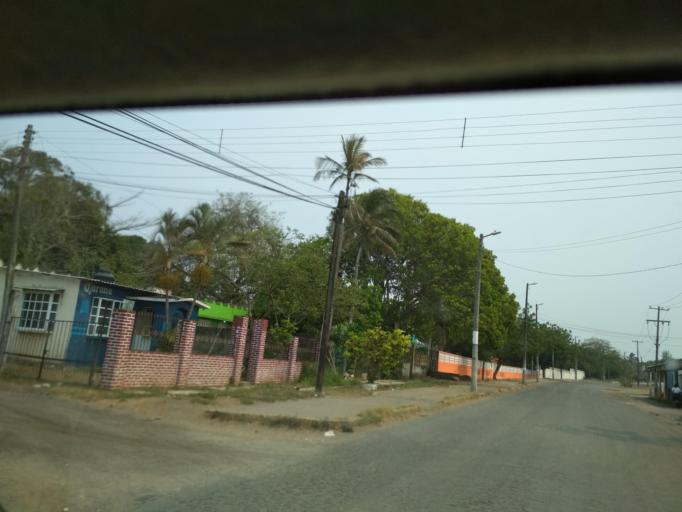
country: MX
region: Veracruz
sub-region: Veracruz
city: Delfino Victoria (Santa Fe)
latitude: 19.2037
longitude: -96.2743
